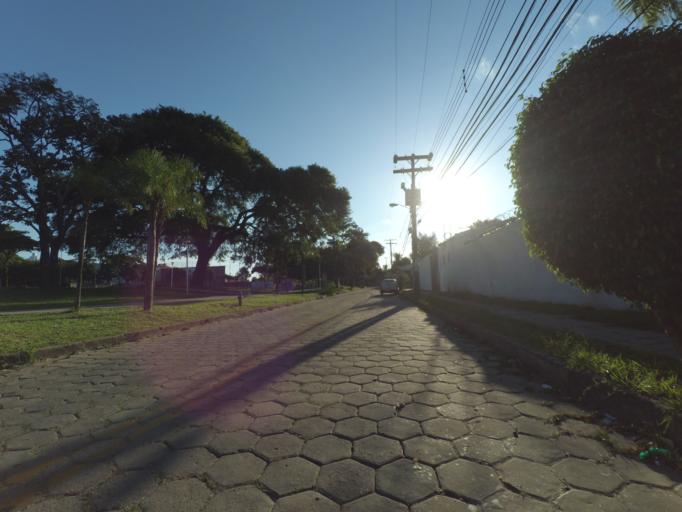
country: BO
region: Santa Cruz
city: Santa Cruz de la Sierra
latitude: -17.7953
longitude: -63.1974
